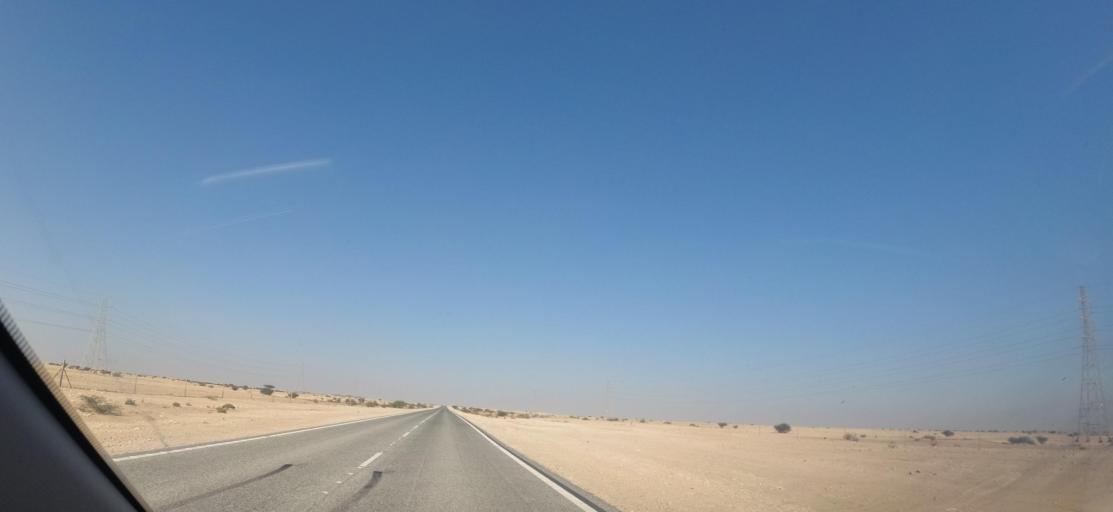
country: QA
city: Al Jumayliyah
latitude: 25.6442
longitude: 51.1065
